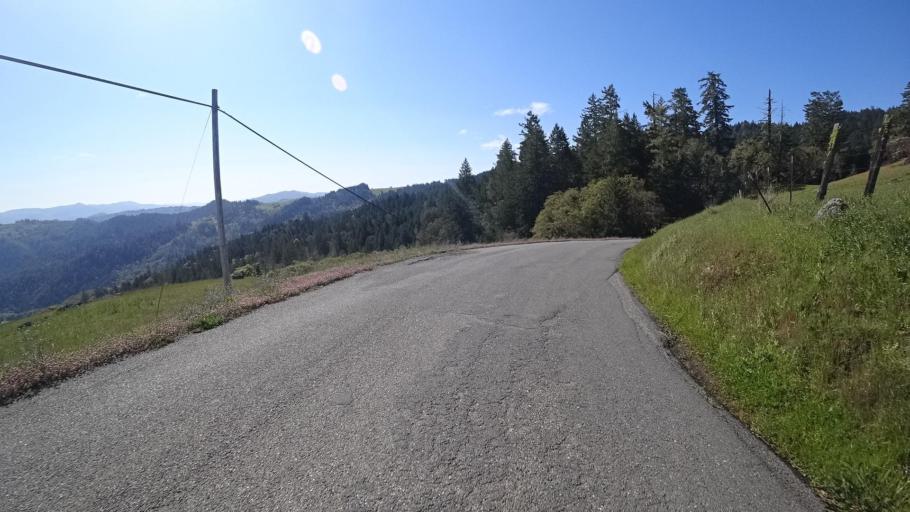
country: US
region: California
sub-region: Humboldt County
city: Redway
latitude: 40.0798
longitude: -123.6536
